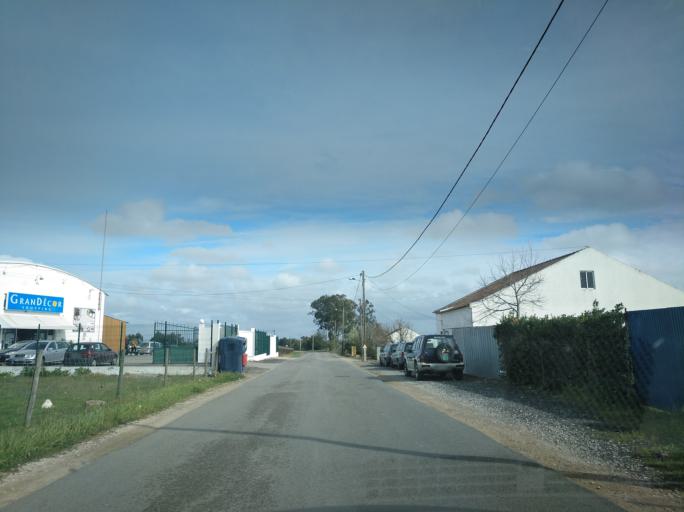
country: PT
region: Setubal
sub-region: Grandola
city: Grandola
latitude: 38.1878
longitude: -8.5626
